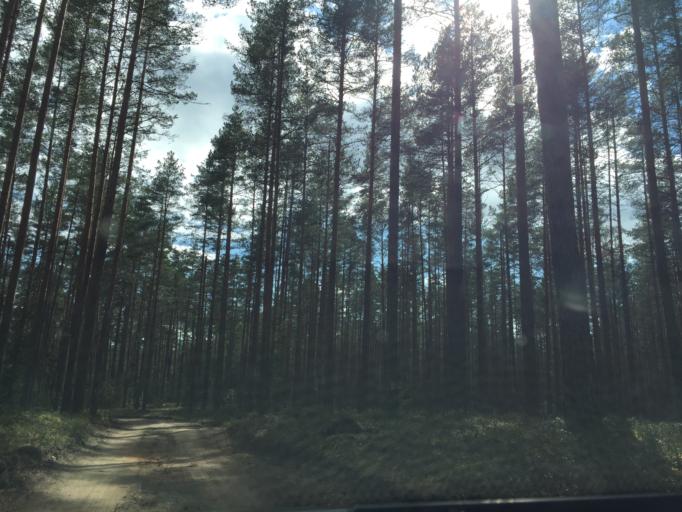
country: LV
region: Gulbenes Rajons
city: Gulbene
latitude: 57.2689
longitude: 26.5502
